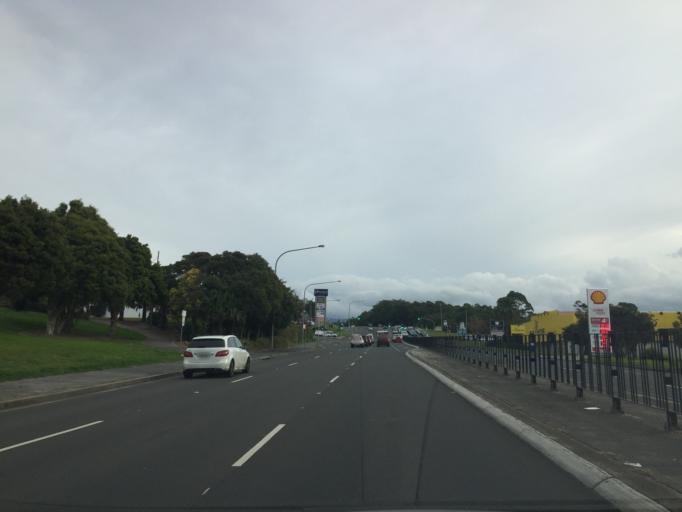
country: AU
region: New South Wales
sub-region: Shellharbour
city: Barrack Heights
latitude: -34.5633
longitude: 150.8322
